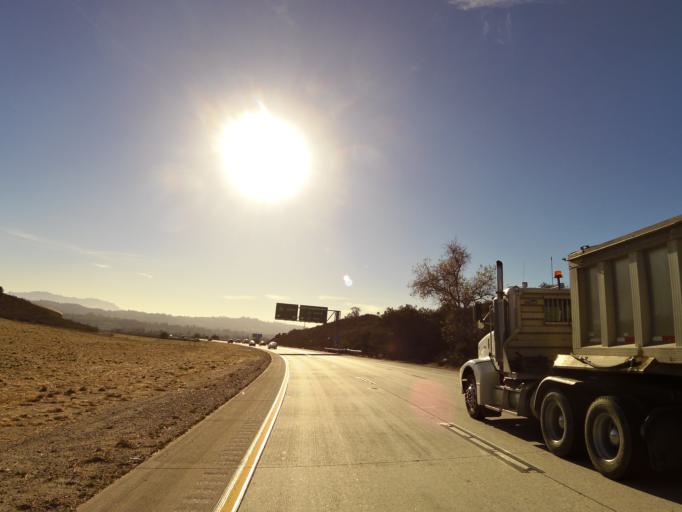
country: US
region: California
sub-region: Ventura County
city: Moorpark
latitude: 34.2915
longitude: -118.8627
